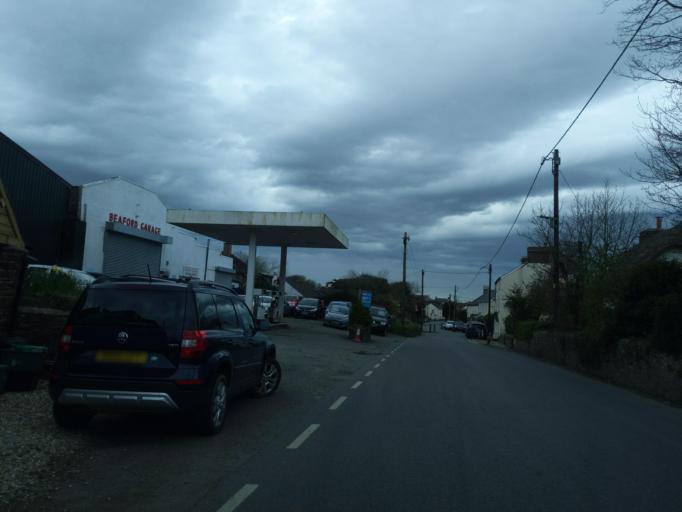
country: GB
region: England
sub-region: Devon
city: Great Torrington
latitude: 50.9150
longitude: -4.0562
